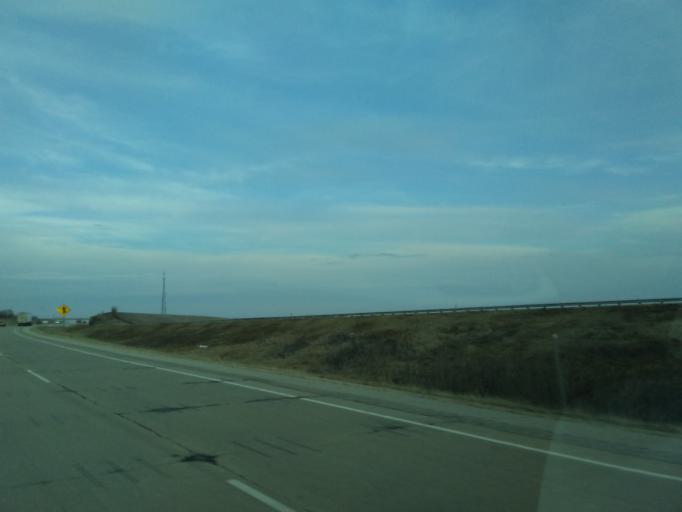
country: US
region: Wisconsin
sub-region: Dane County
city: Mount Horeb
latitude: 43.0046
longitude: -89.7013
